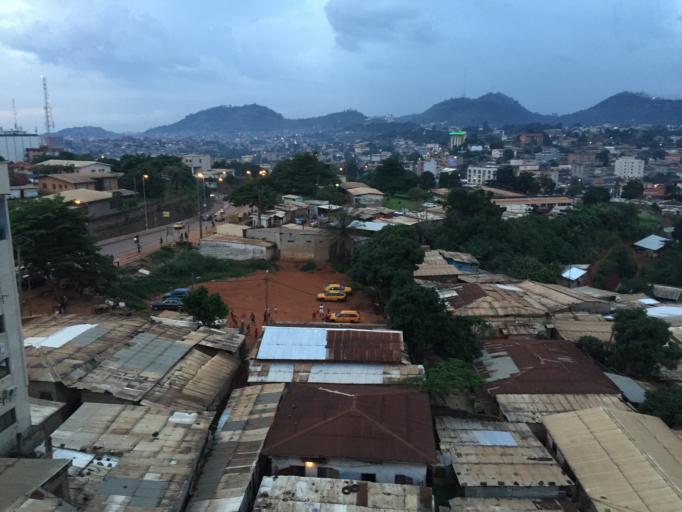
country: CM
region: Centre
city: Yaounde
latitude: 3.8829
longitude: 11.5233
